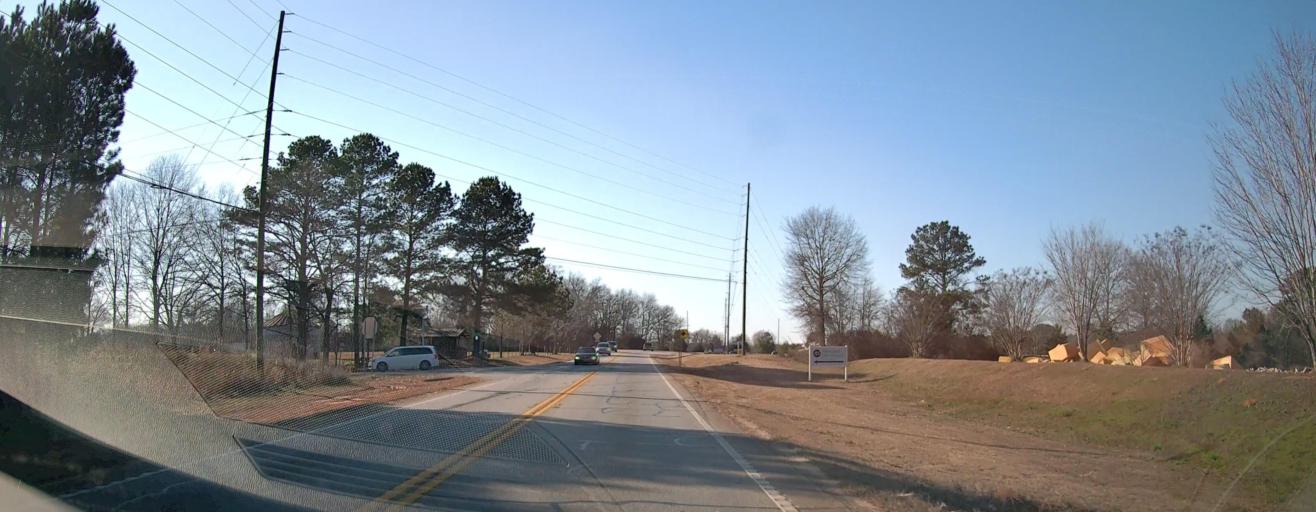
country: US
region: Georgia
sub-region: Henry County
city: Locust Grove
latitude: 33.3204
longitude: -84.0576
